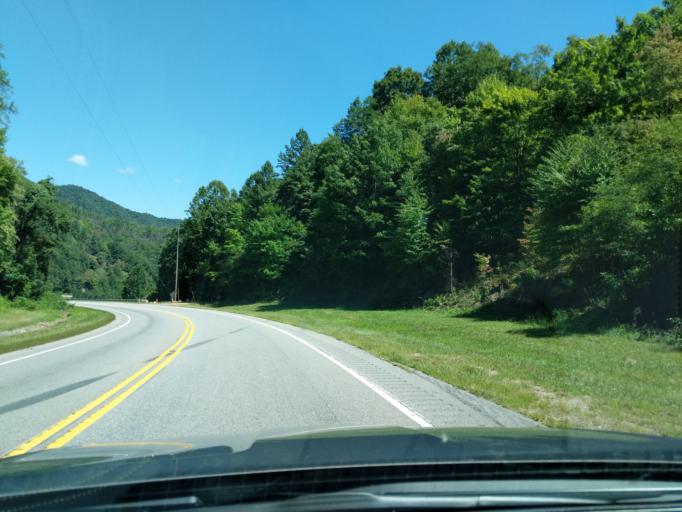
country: US
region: North Carolina
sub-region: Macon County
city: Franklin
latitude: 35.1316
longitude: -83.5147
